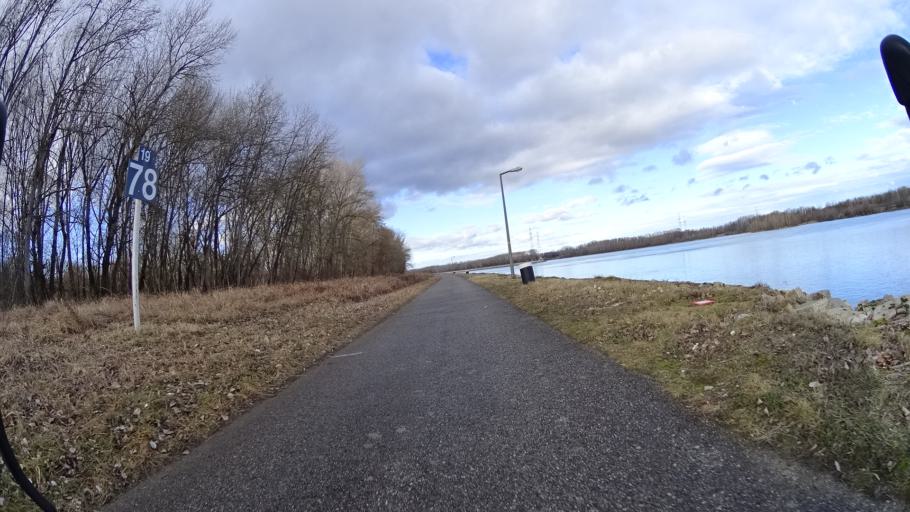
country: AT
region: Lower Austria
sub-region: Politischer Bezirk Tulln
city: Kirchberg am Wagram
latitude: 48.3664
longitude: 15.8753
